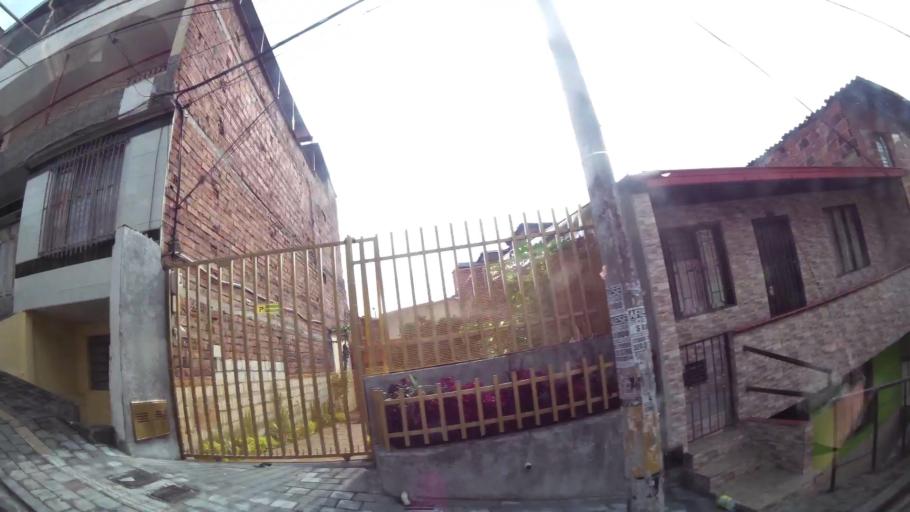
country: CO
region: Antioquia
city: Sabaneta
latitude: 6.1671
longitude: -75.6254
